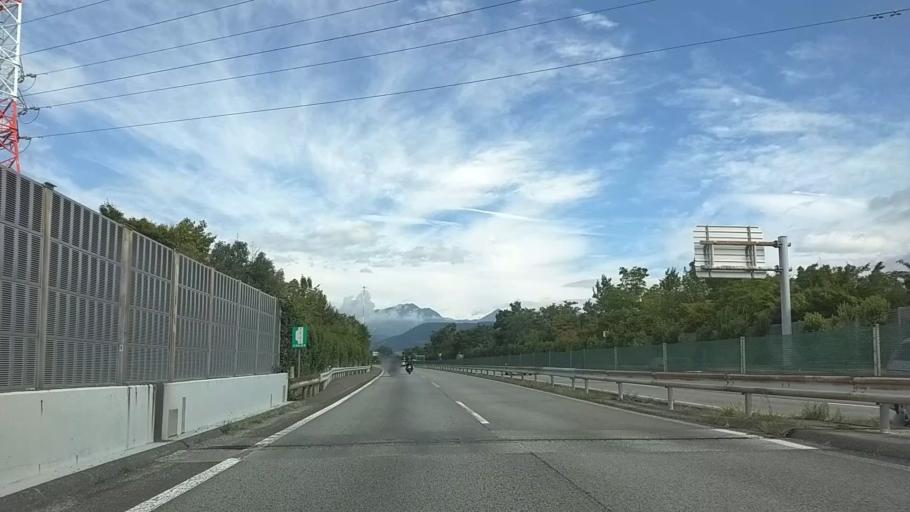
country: JP
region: Yamanashi
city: Kofu-shi
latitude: 35.6500
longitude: 138.5372
